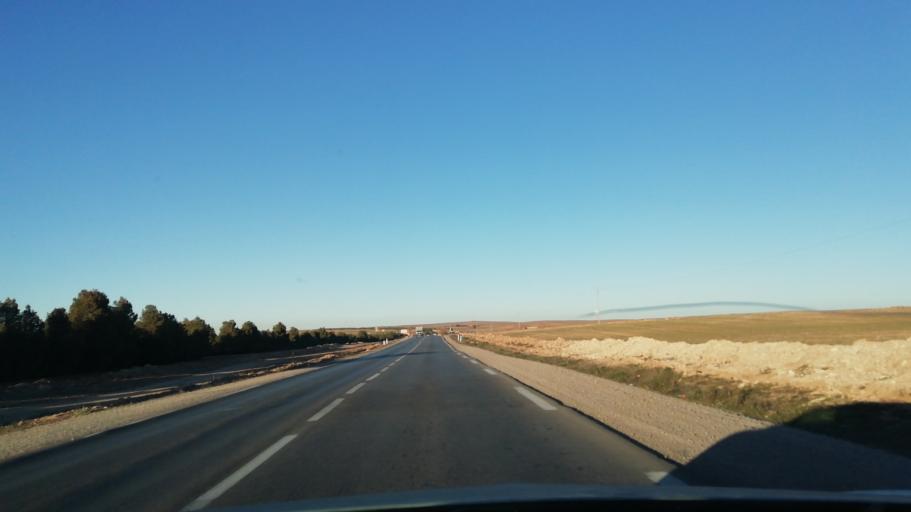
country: DZ
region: Saida
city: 'Ain el Hadjar
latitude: 34.5663
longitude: 0.1219
